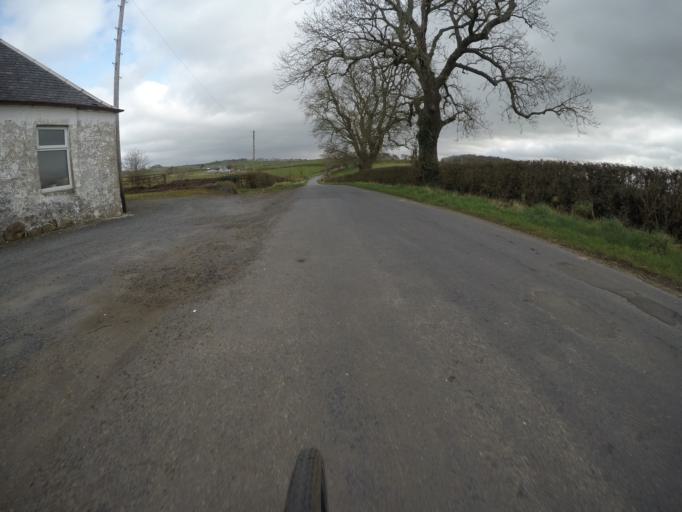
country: GB
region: Scotland
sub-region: East Ayrshire
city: Stewarton
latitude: 55.6722
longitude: -4.5569
